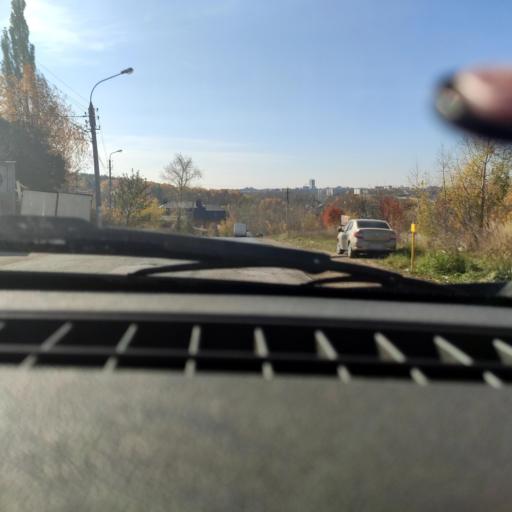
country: RU
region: Bashkortostan
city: Ufa
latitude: 54.8349
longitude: 56.1428
